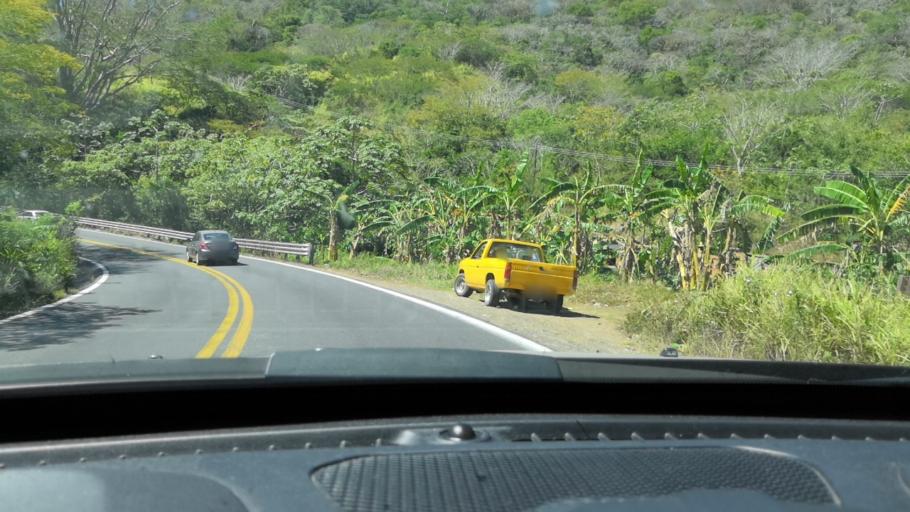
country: MX
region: Nayarit
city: Compostela
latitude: 21.2164
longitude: -104.9855
